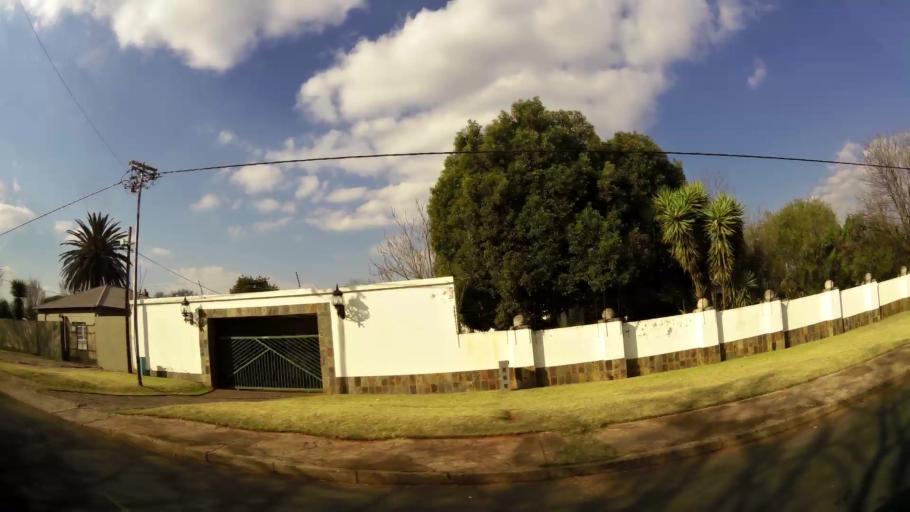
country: ZA
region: Gauteng
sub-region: West Rand District Municipality
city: Krugersdorp
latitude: -26.0864
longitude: 27.7728
